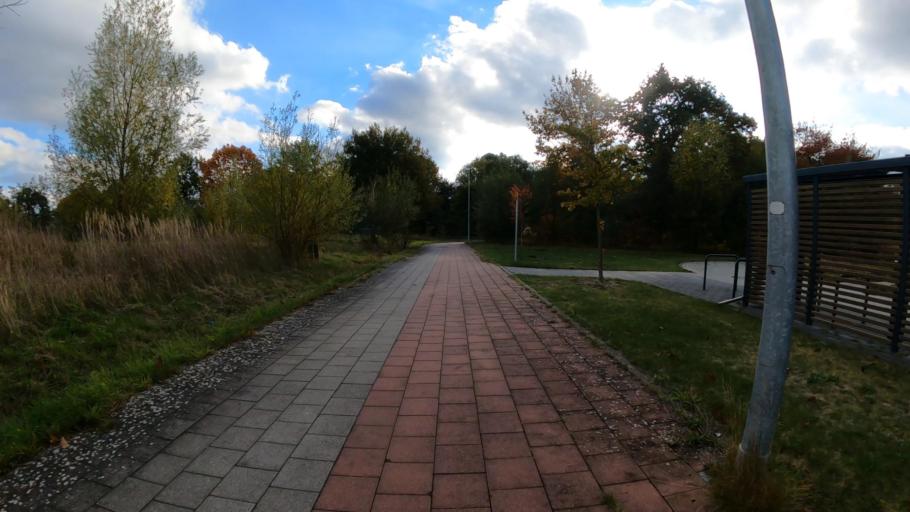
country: DE
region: Schleswig-Holstein
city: Delingsdorf
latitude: 53.6770
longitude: 10.2528
